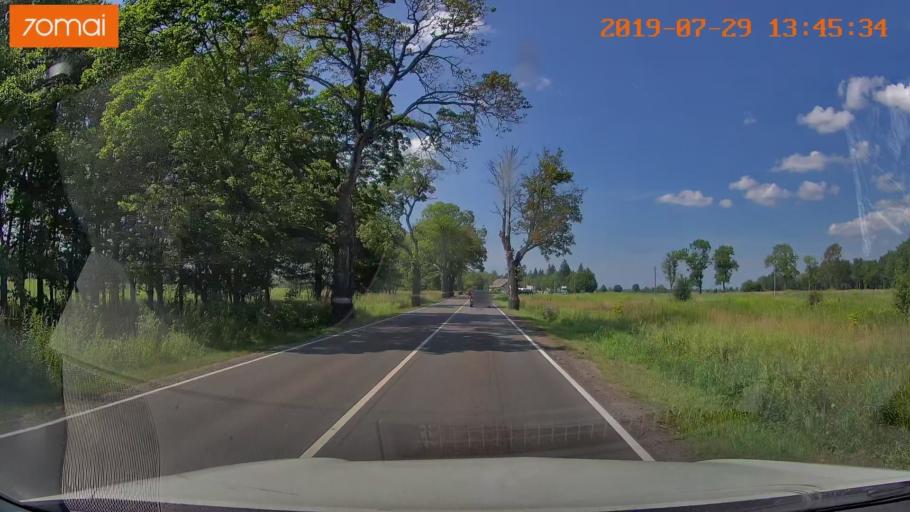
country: RU
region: Kaliningrad
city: Primorsk
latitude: 54.7397
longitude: 20.0720
